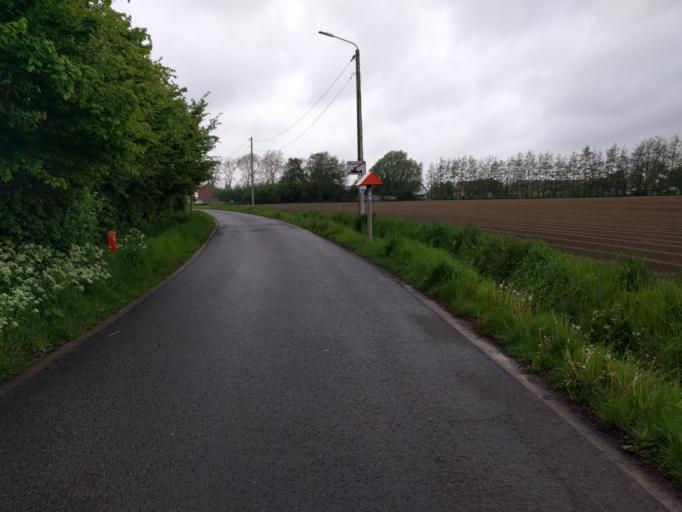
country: BE
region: Flanders
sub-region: Provincie West-Vlaanderen
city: Wevelgem
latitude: 50.8122
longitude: 3.1597
